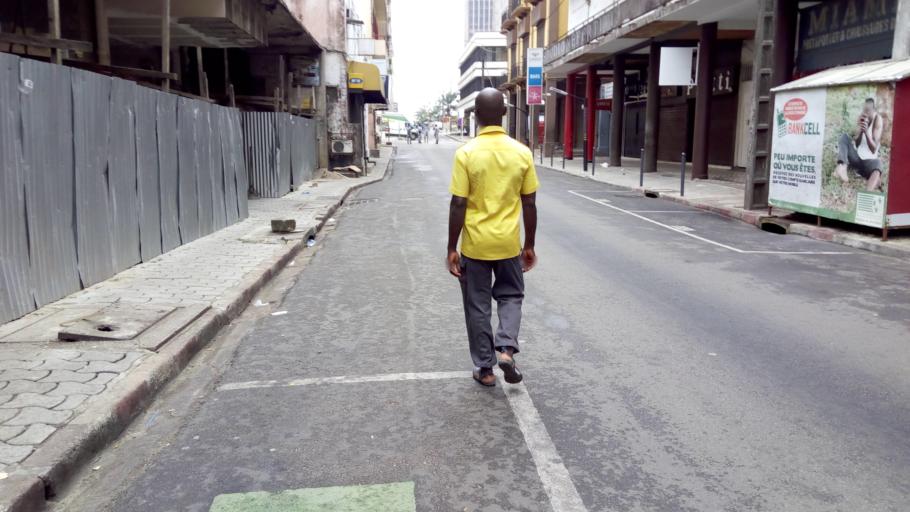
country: CI
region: Lagunes
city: Abidjan
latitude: 5.3222
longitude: -4.0189
